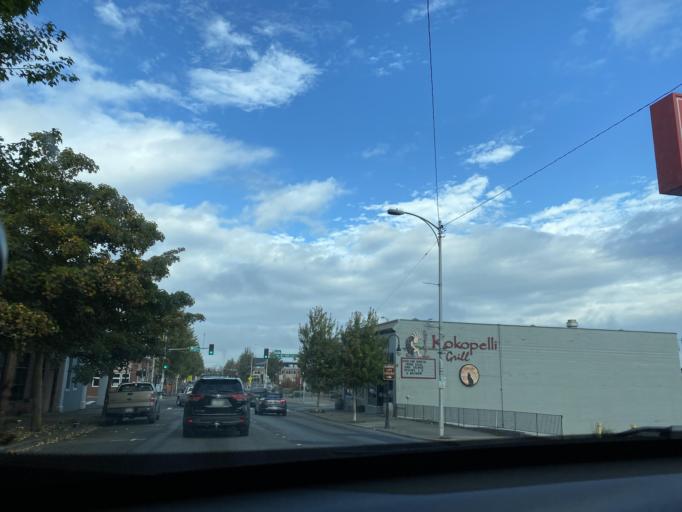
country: US
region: Washington
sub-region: Clallam County
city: Port Angeles
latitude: 48.1188
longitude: -123.4301
